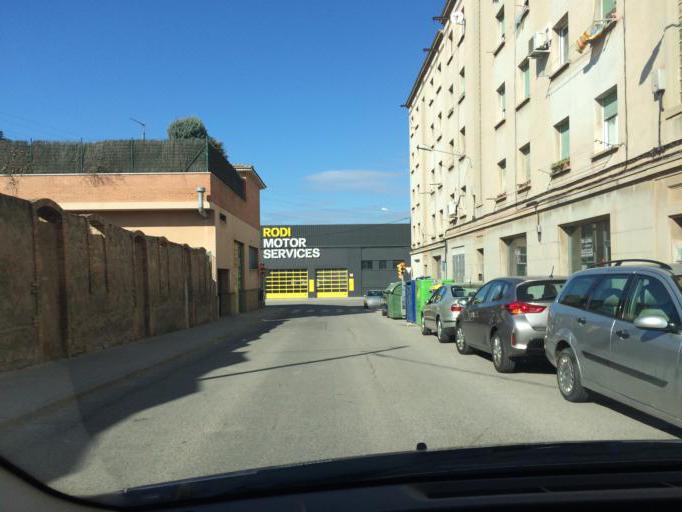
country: ES
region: Catalonia
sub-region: Provincia de Barcelona
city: Manresa
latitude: 41.7330
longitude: 1.8396
